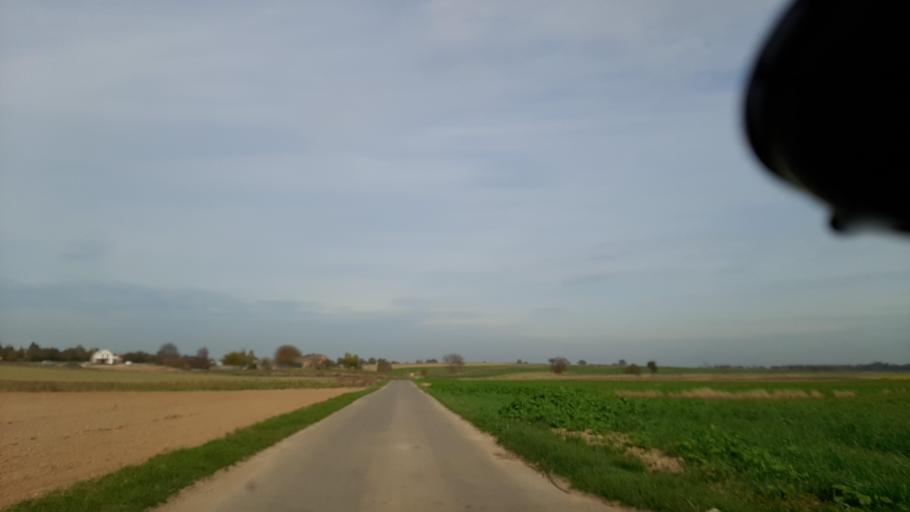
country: PL
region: Lublin Voivodeship
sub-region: Powiat lubelski
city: Jastkow
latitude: 51.3286
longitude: 22.4080
